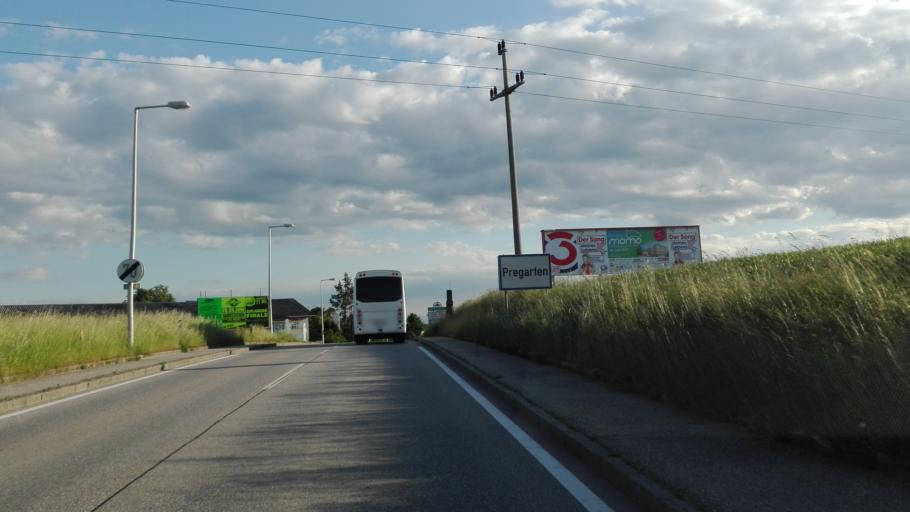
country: AT
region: Upper Austria
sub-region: Politischer Bezirk Urfahr-Umgebung
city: Engerwitzdorf
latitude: 48.3646
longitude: 14.5364
